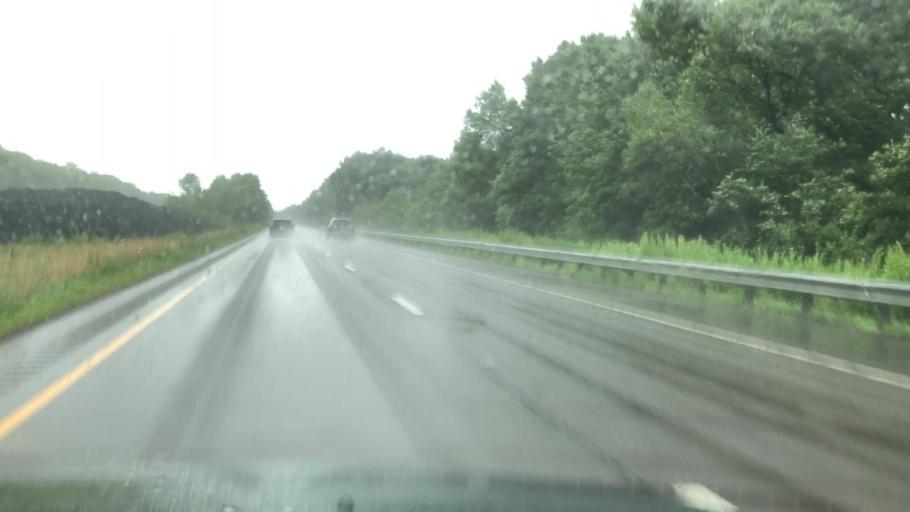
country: US
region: Pennsylvania
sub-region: Pike County
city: Gold Key Lake
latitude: 41.3453
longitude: -74.9260
